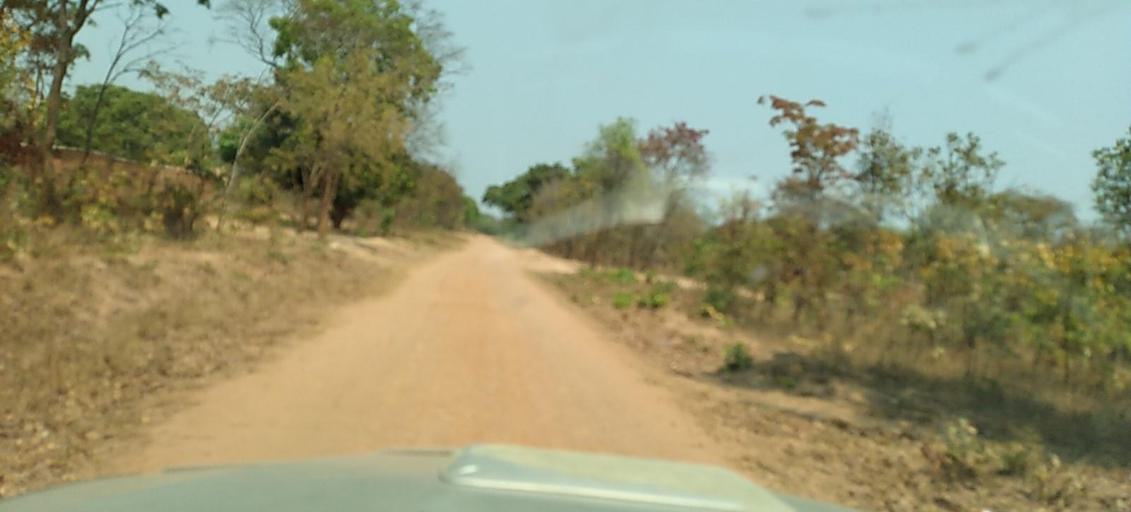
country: ZM
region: North-Western
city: Kasempa
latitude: -13.6933
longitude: 26.3250
